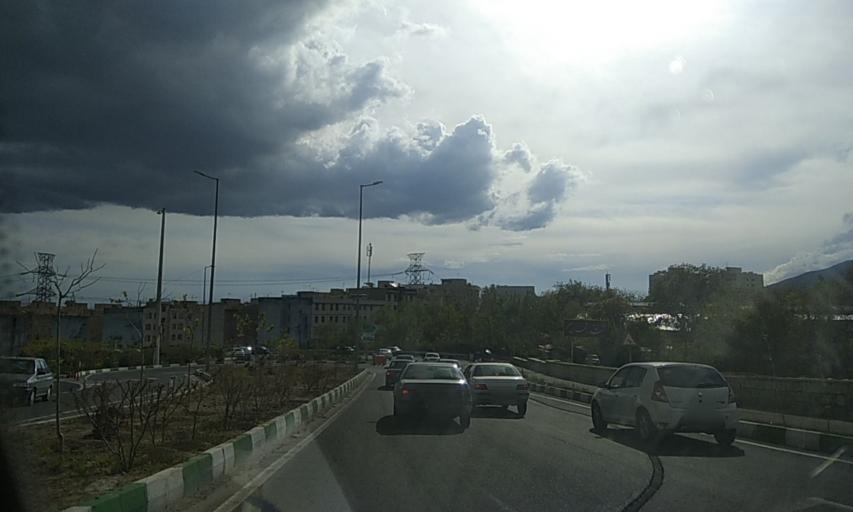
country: IR
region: Tehran
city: Tajrish
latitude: 35.7750
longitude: 51.2999
